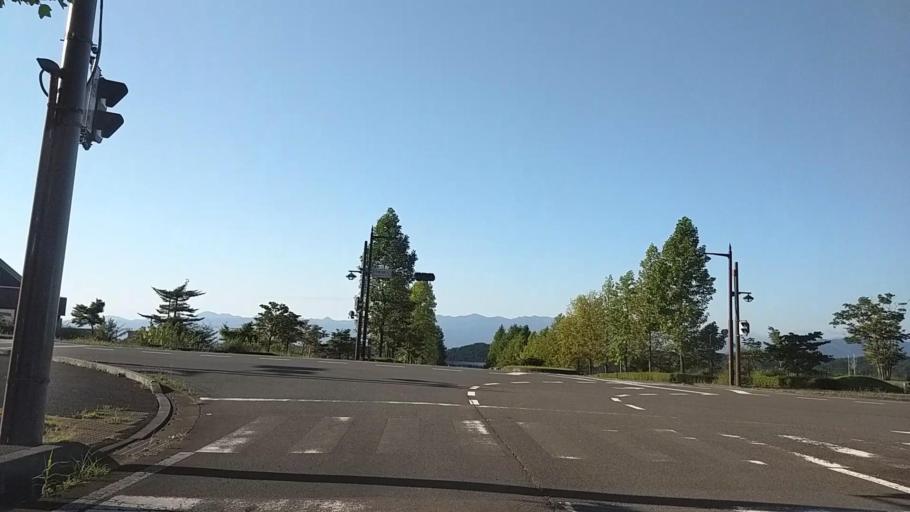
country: JP
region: Gunma
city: Annaka
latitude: 36.3609
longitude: 138.8494
